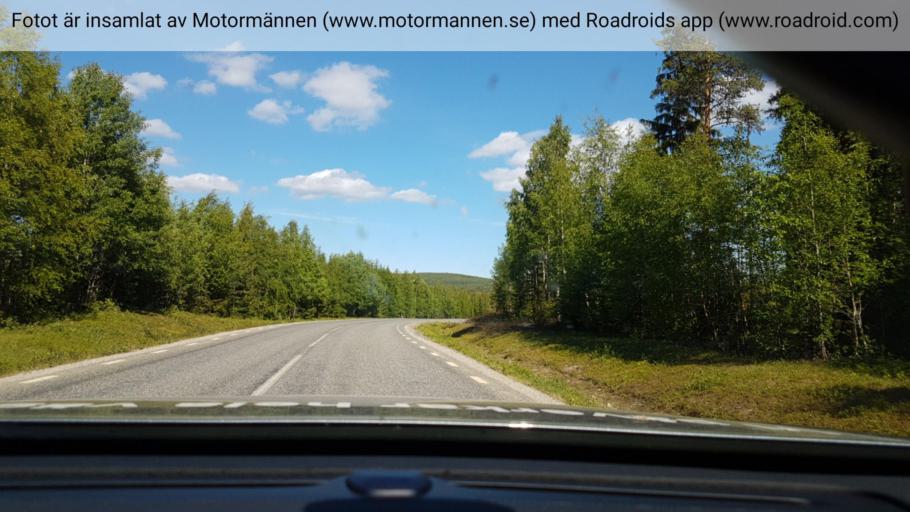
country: SE
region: Vaesterbotten
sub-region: Lycksele Kommun
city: Lycksele
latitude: 64.6221
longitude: 18.4108
